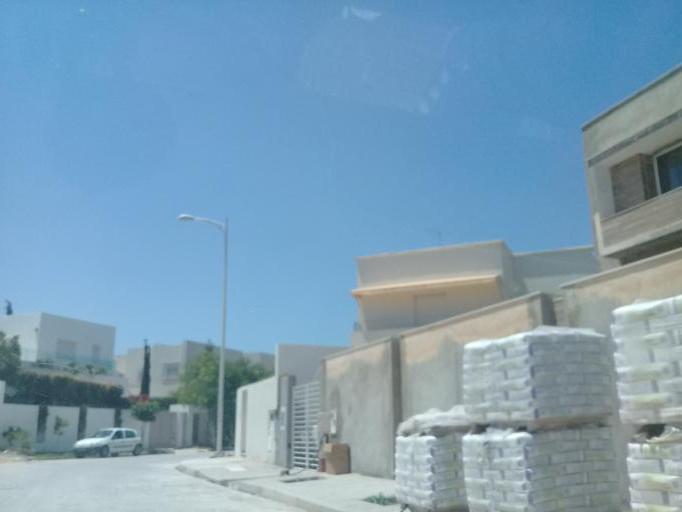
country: TN
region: Tunis
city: La Goulette
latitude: 36.8433
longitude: 10.2666
